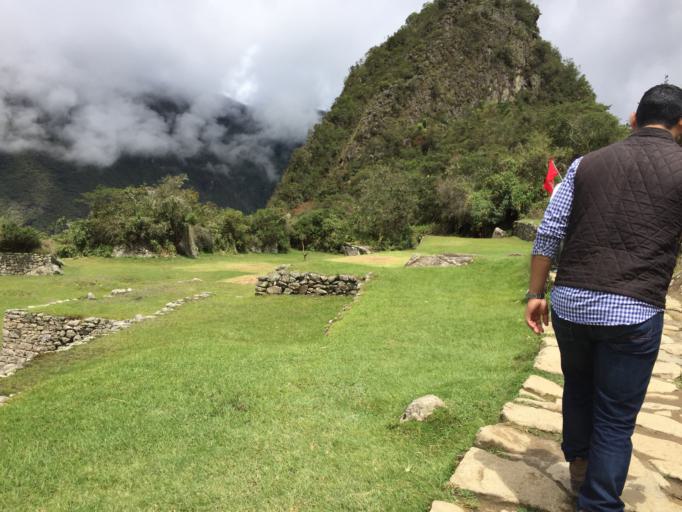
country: PE
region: Cusco
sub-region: Provincia de La Convencion
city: Santa Teresa
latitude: -13.1622
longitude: -72.5457
